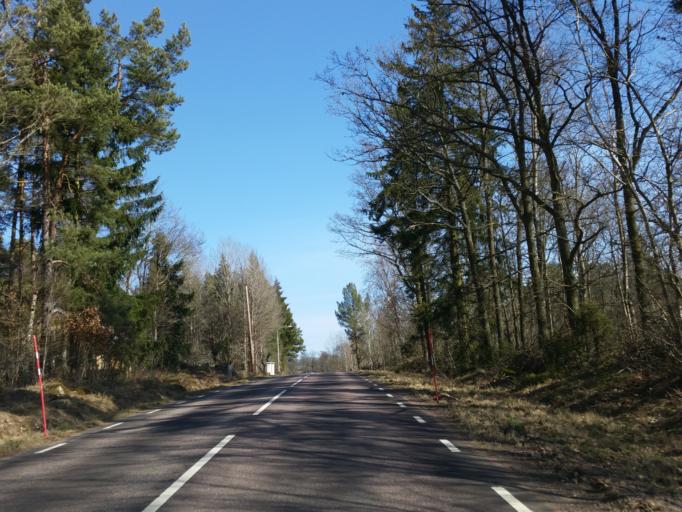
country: SE
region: Kalmar
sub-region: Monsteras Kommun
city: Timmernabben
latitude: 56.8591
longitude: 16.4050
